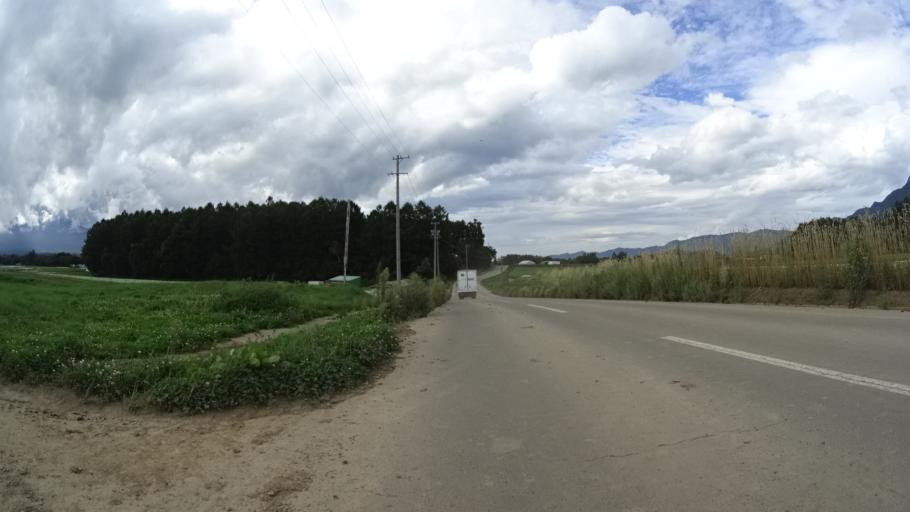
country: JP
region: Nagano
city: Saku
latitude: 35.9680
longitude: 138.5158
